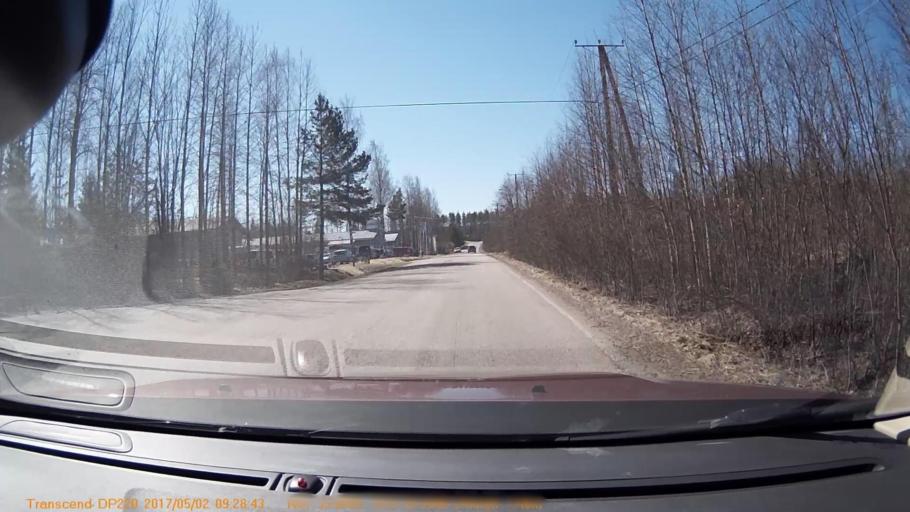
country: FI
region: Pirkanmaa
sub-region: Tampere
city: Yloejaervi
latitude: 61.5649
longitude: 23.5375
